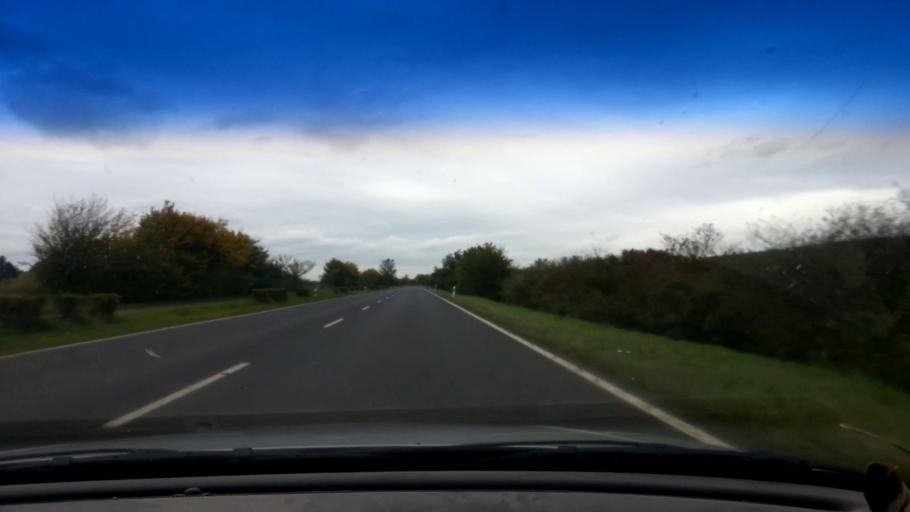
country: DE
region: Bavaria
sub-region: Upper Franconia
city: Baunach
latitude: 49.9940
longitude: 10.8416
